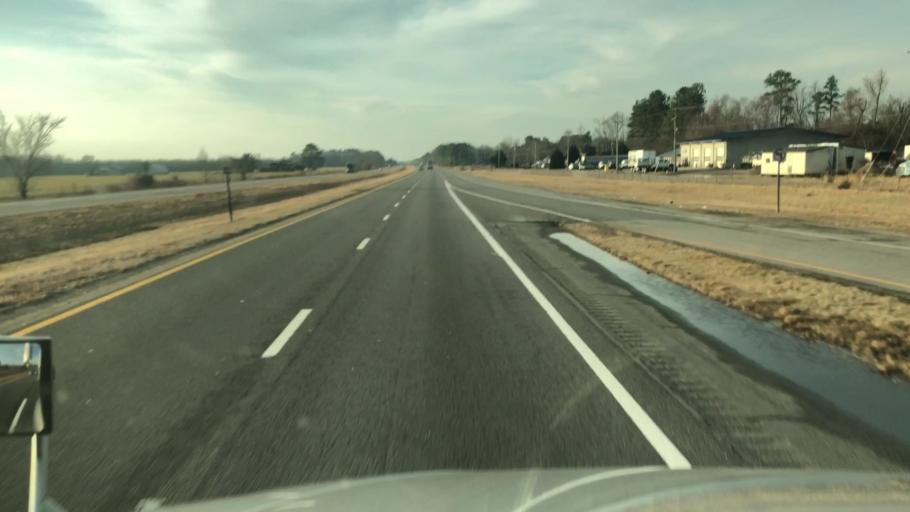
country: US
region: Virginia
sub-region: Sussex County
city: Sussex
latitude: 36.9405
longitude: -77.3929
